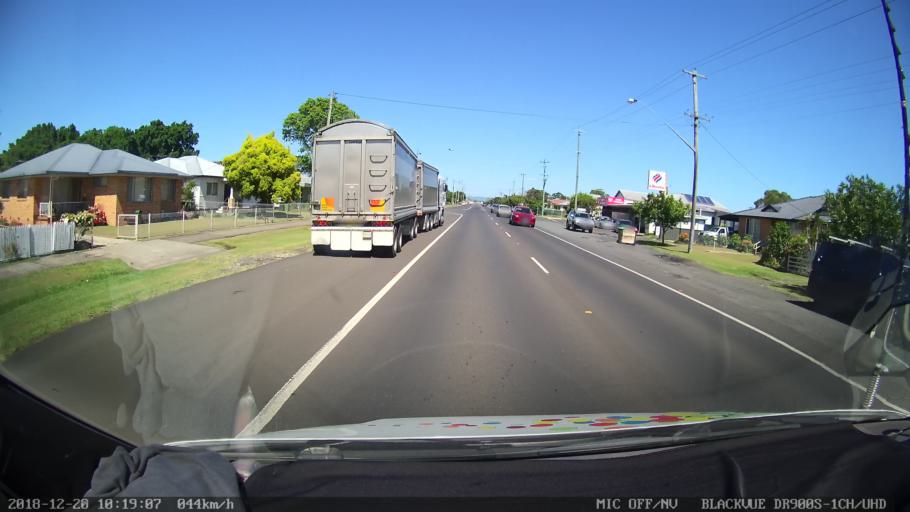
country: AU
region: New South Wales
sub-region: Richmond Valley
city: Casino
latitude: -28.8600
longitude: 153.0568
